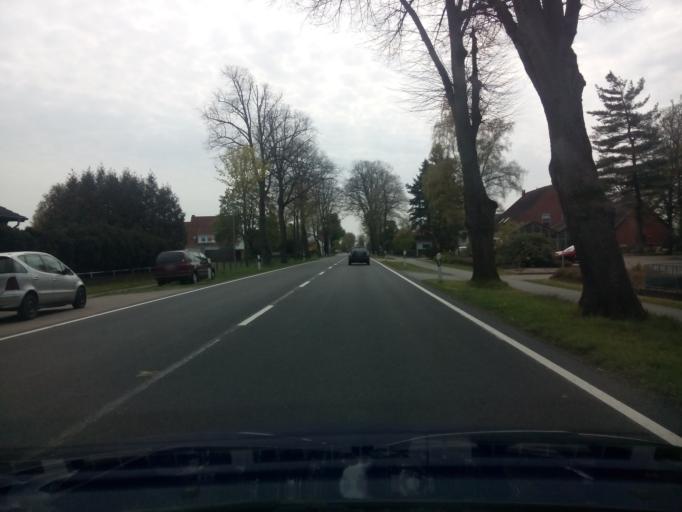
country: DE
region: Lower Saxony
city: Stuhr
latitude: 52.9941
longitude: 8.7870
